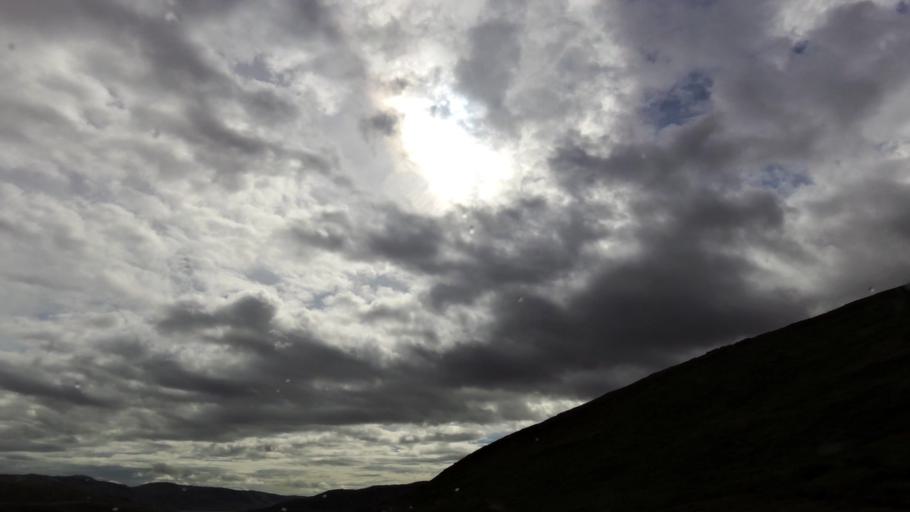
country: IS
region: West
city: Stykkisholmur
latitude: 65.6029
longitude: -22.1064
